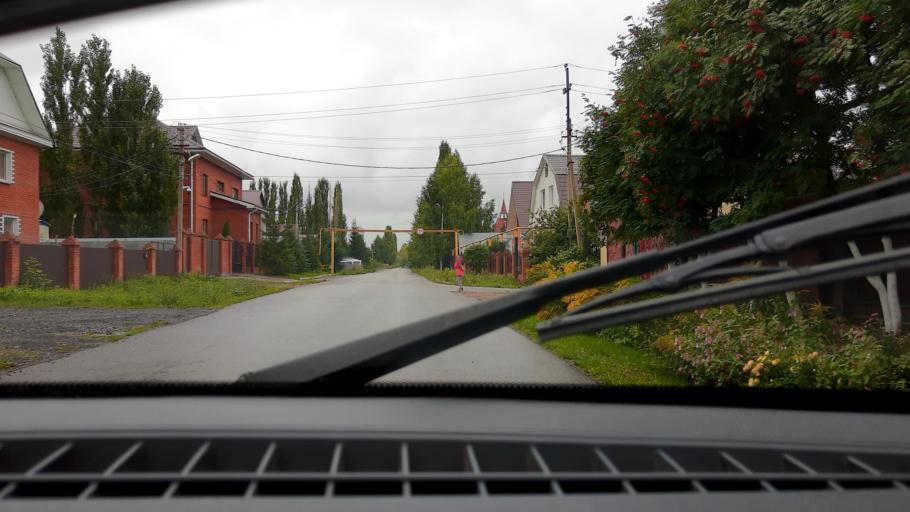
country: RU
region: Bashkortostan
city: Mikhaylovka
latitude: 54.7892
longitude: 55.8960
